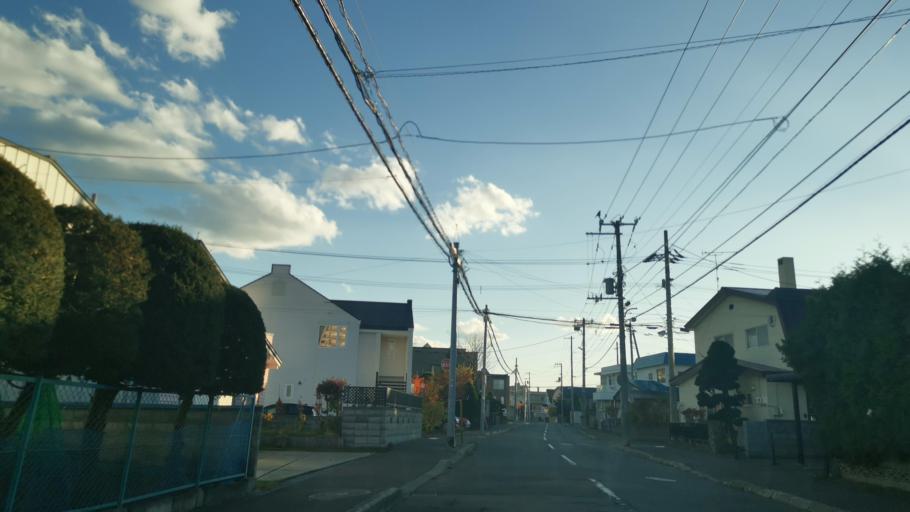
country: JP
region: Hokkaido
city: Sapporo
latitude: 43.0124
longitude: 141.3699
